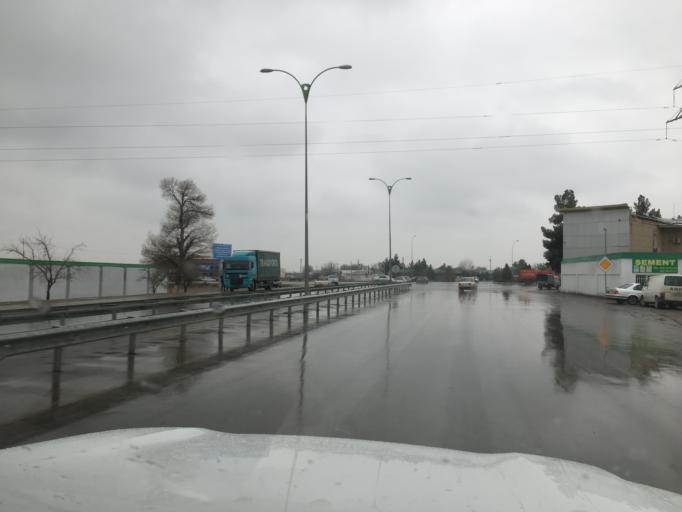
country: TM
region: Mary
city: Mary
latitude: 37.5712
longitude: 61.8339
